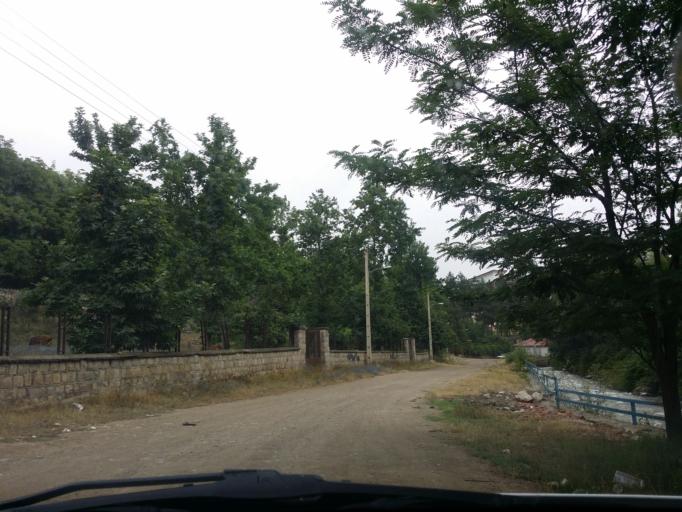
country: IR
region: Mazandaran
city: `Abbasabad
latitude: 36.5051
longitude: 51.1547
